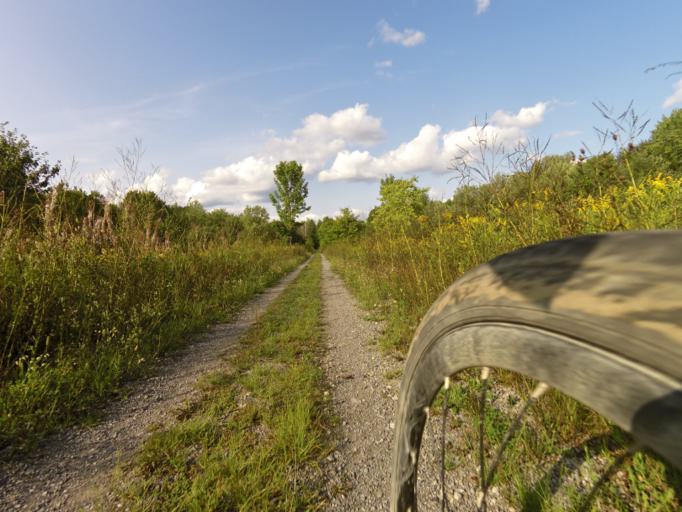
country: CA
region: Ontario
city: Kingston
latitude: 44.4458
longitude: -76.5273
